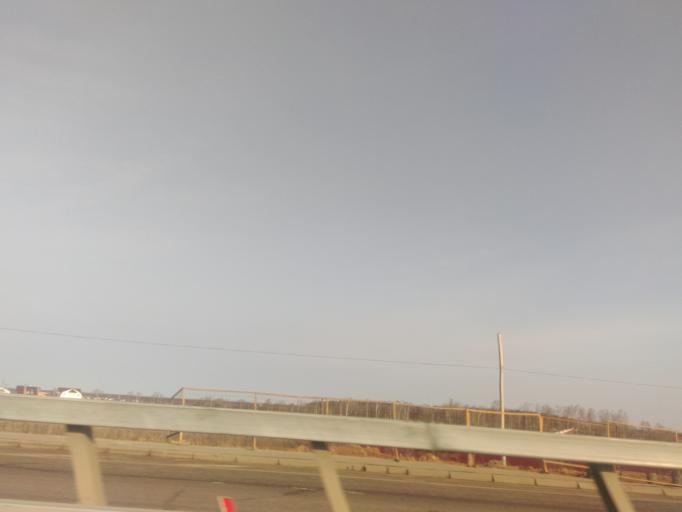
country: RU
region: Moscow
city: Vnukovo
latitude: 55.5911
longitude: 37.2274
